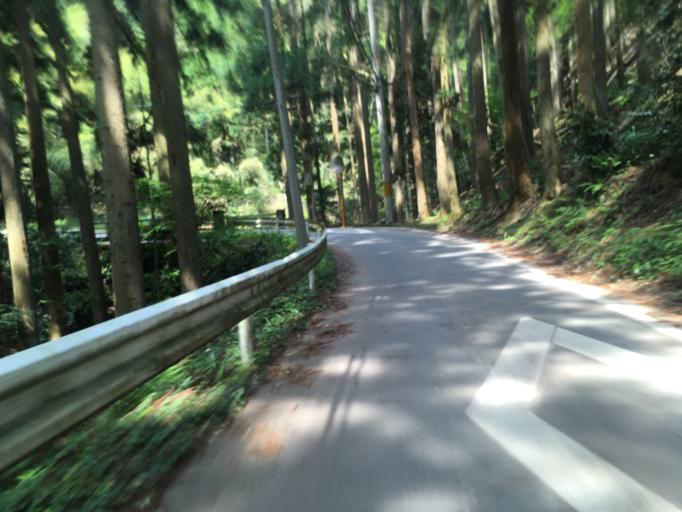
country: JP
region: Kyoto
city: Kameoka
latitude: 35.0738
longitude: 135.6119
